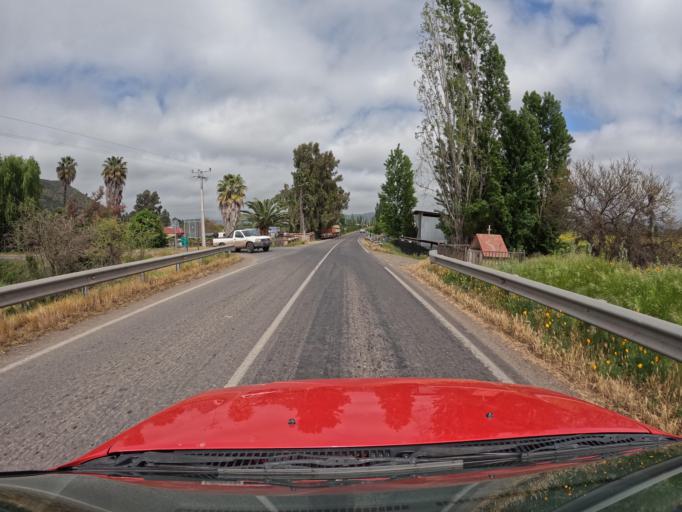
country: CL
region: O'Higgins
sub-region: Provincia de Colchagua
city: Santa Cruz
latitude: -34.6766
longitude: -71.3555
